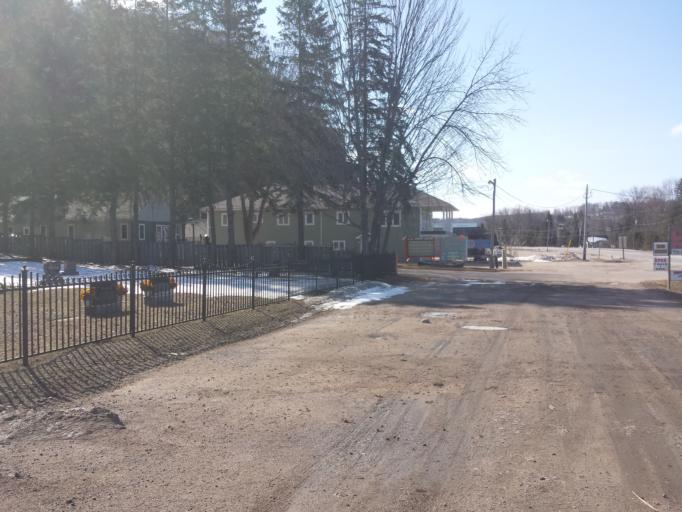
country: CA
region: Ontario
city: Bancroft
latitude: 45.0714
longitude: -77.8627
